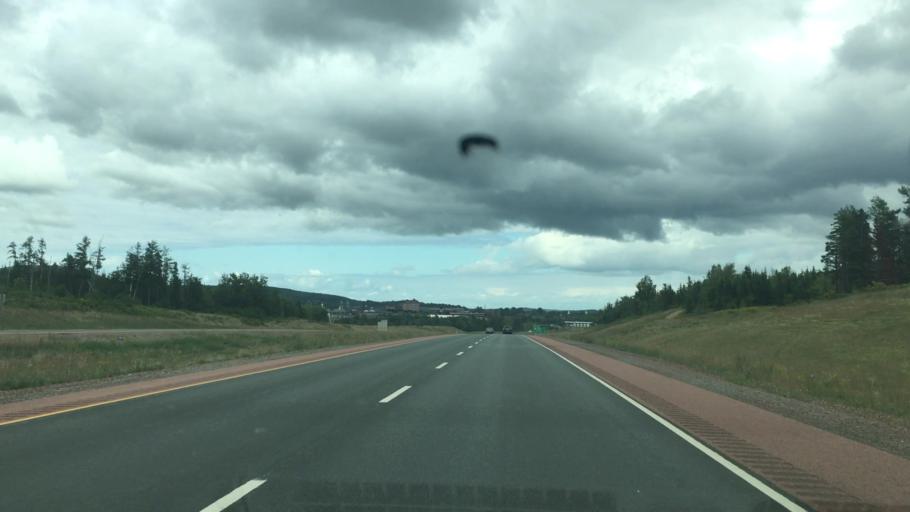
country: CA
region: Nova Scotia
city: Antigonish
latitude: 45.6076
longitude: -62.0106
